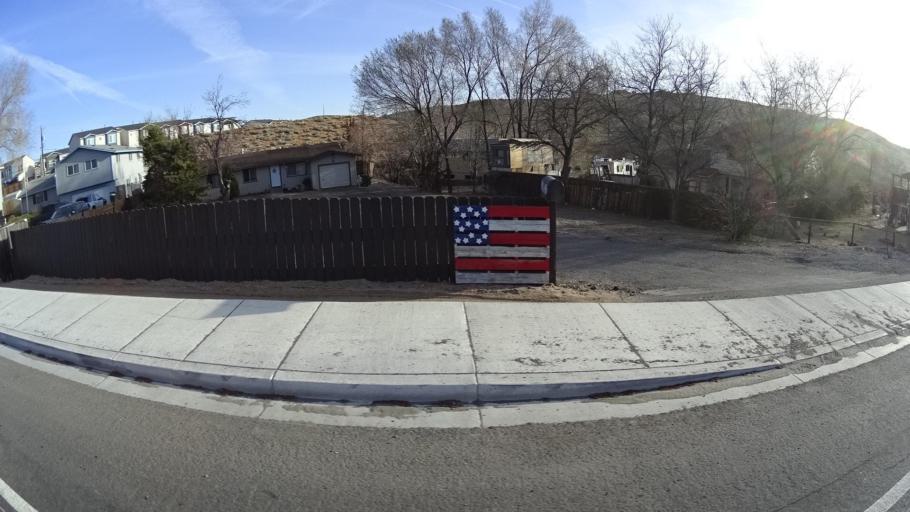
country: US
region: Nevada
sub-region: Washoe County
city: Sun Valley
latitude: 39.5669
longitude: -119.7762
